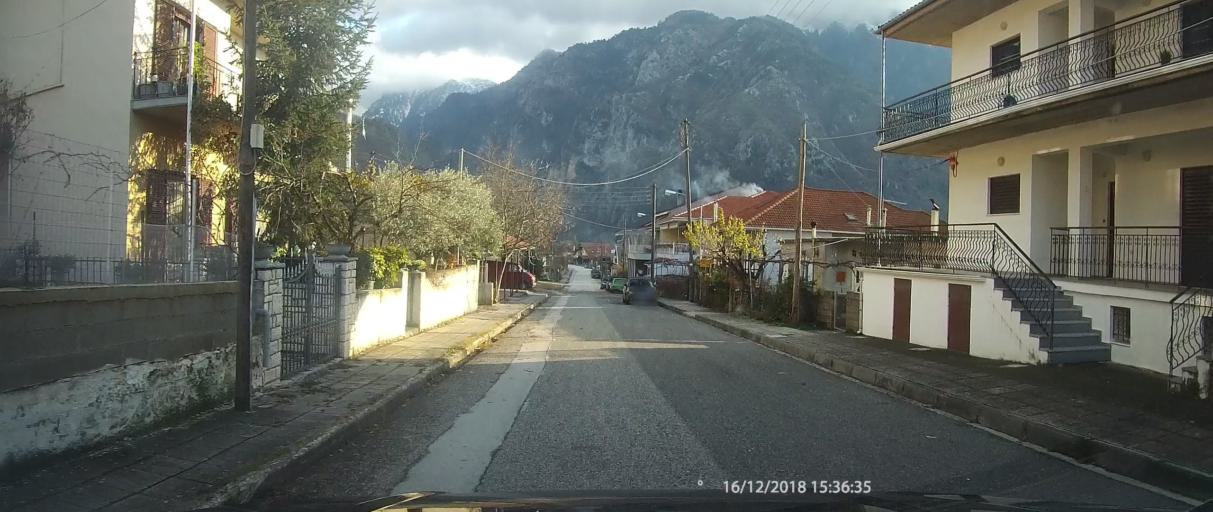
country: GR
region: Epirus
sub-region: Nomos Ioanninon
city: Konitsa
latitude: 40.0457
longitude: 20.7404
